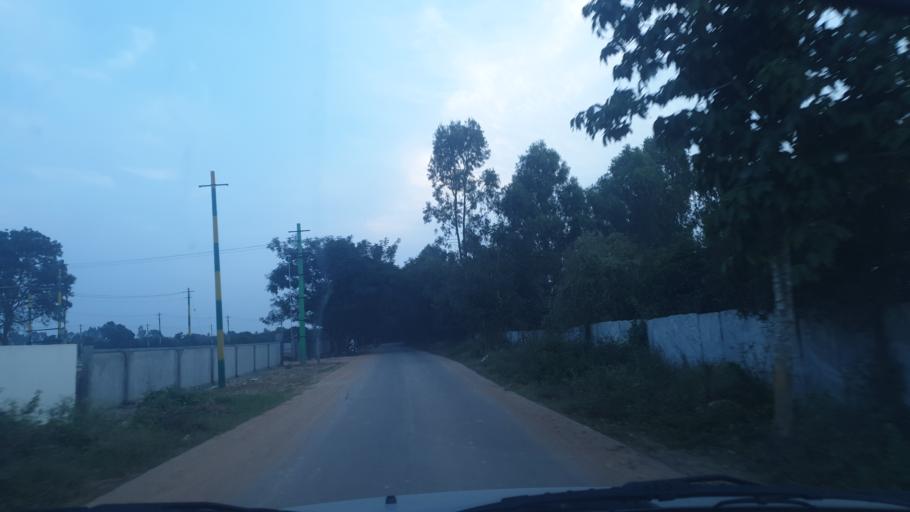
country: IN
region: Karnataka
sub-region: Bangalore Rural
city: Hoskote
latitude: 13.0847
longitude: 77.7018
